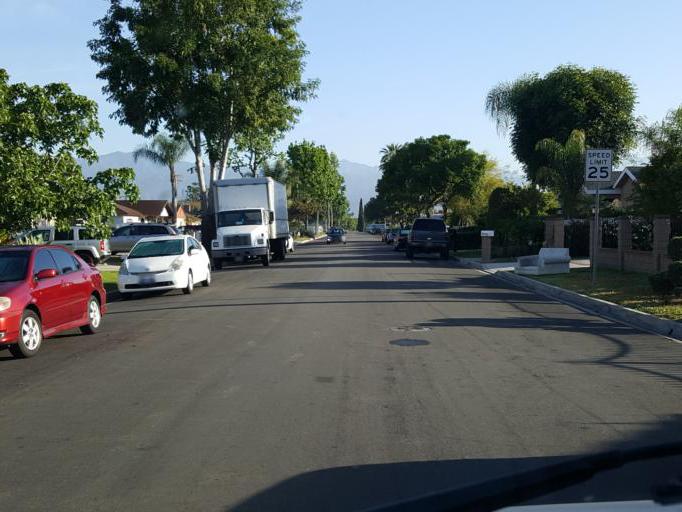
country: US
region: California
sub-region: Los Angeles County
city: Valinda
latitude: 34.0443
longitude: -117.9243
